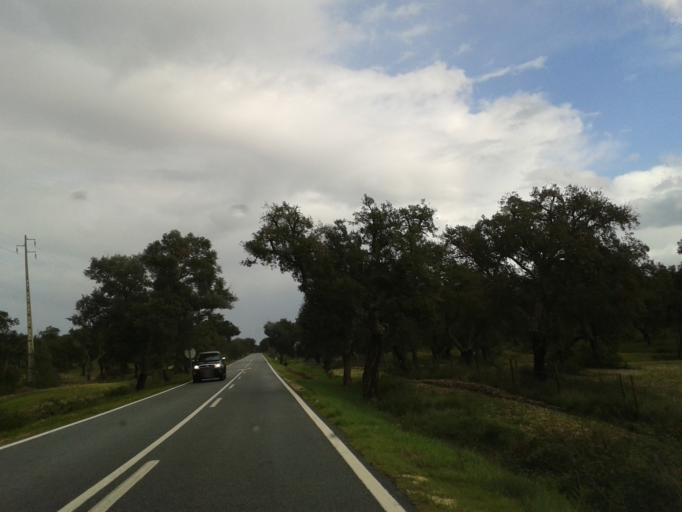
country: PT
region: Santarem
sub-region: Benavente
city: Poceirao
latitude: 38.8177
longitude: -8.7787
